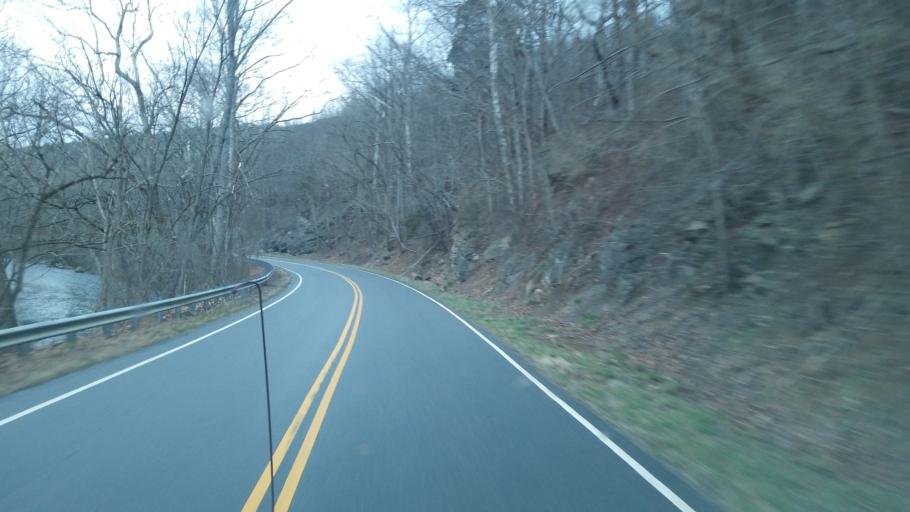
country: US
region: Virginia
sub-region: Giles County
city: Narrows
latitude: 37.1982
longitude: -80.8351
